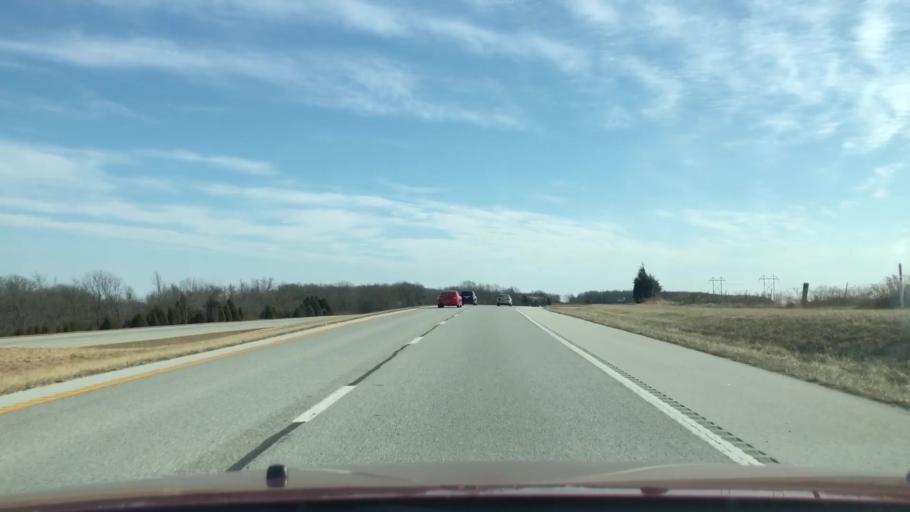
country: US
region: Missouri
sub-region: Webster County
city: Seymour
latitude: 37.1183
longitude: -92.6866
